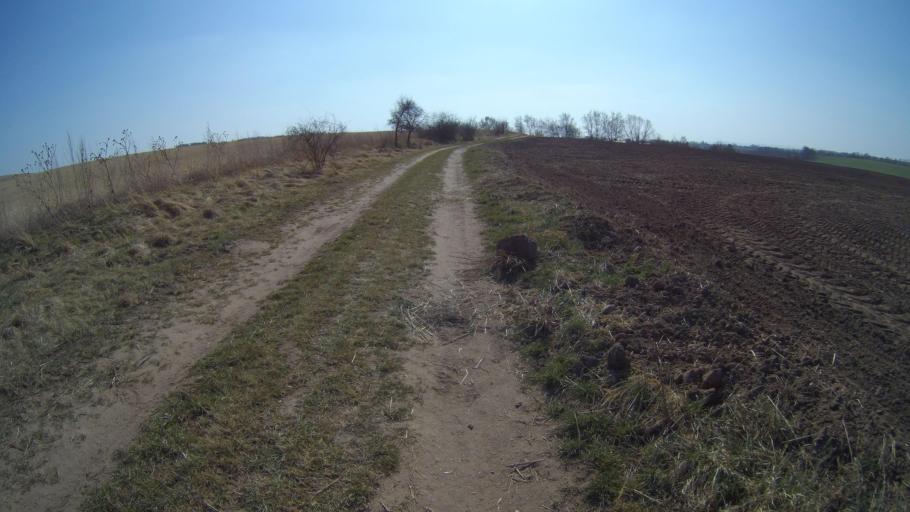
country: CZ
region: Ustecky
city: Mecholupy
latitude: 50.2532
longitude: 13.5334
